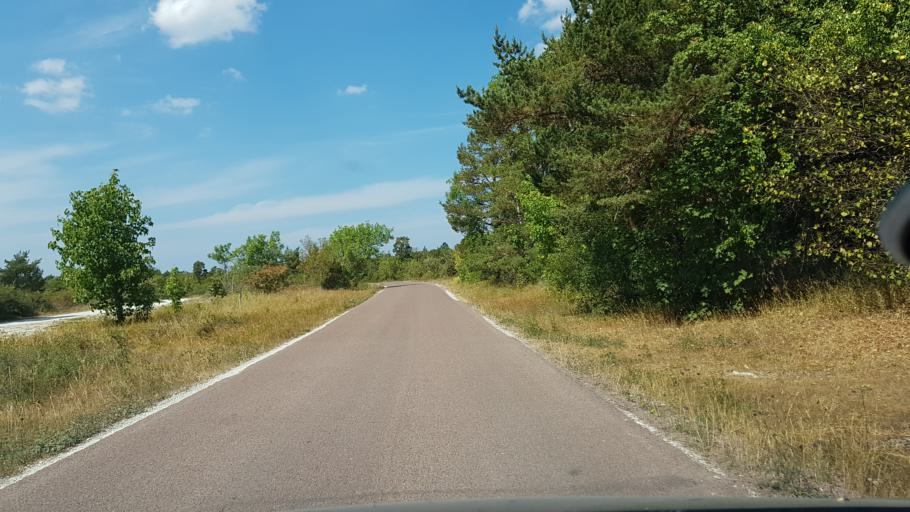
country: SE
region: Gotland
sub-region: Gotland
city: Visby
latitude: 57.6692
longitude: 18.3662
